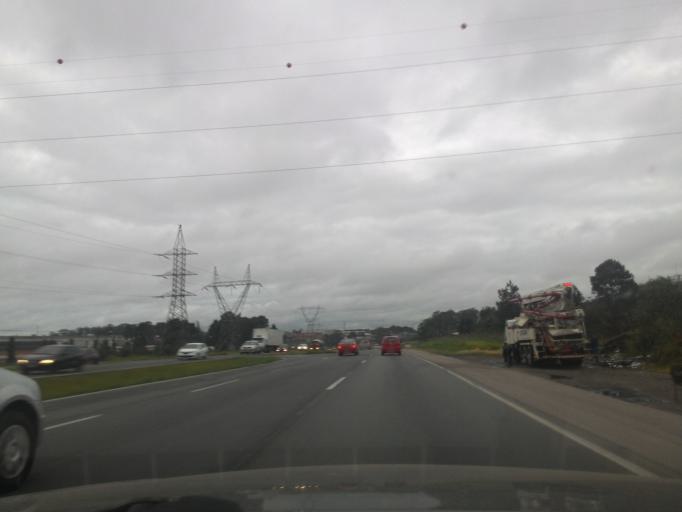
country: BR
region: Parana
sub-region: Araucaria
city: Araucaria
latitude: -25.5482
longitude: -49.3222
